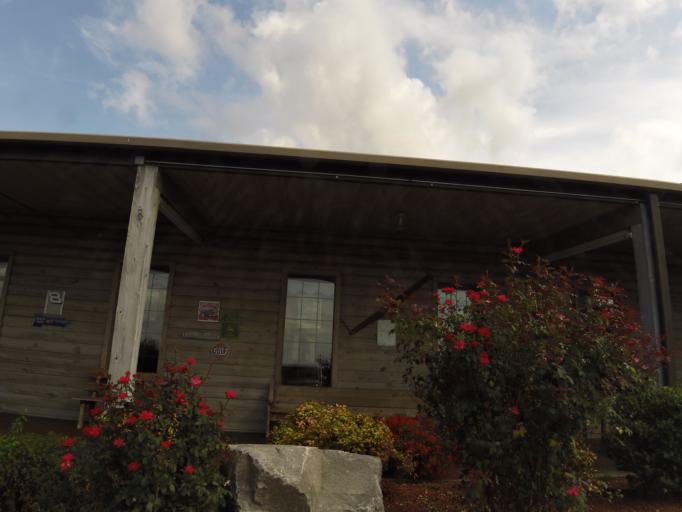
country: US
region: Tennessee
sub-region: Humphreys County
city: Waverly
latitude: 35.8844
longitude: -87.7980
